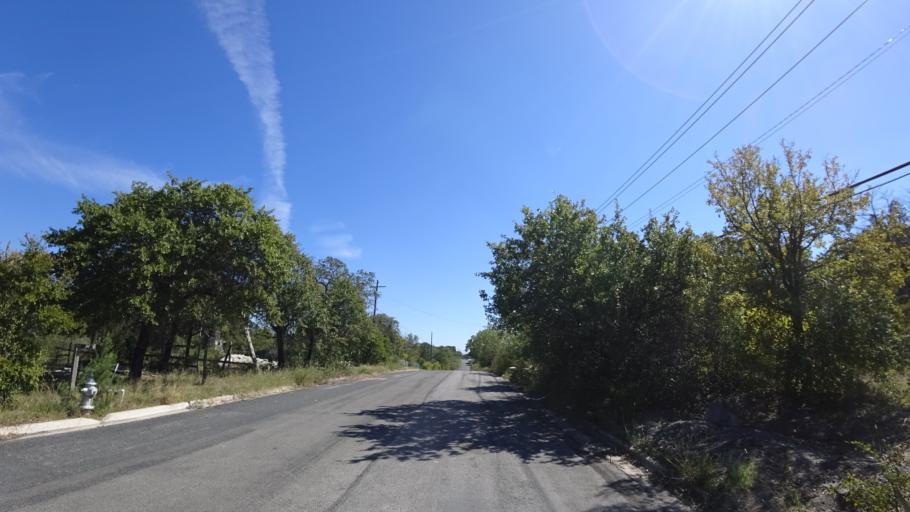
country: US
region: Texas
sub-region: Travis County
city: Austin
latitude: 30.2694
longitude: -97.6760
